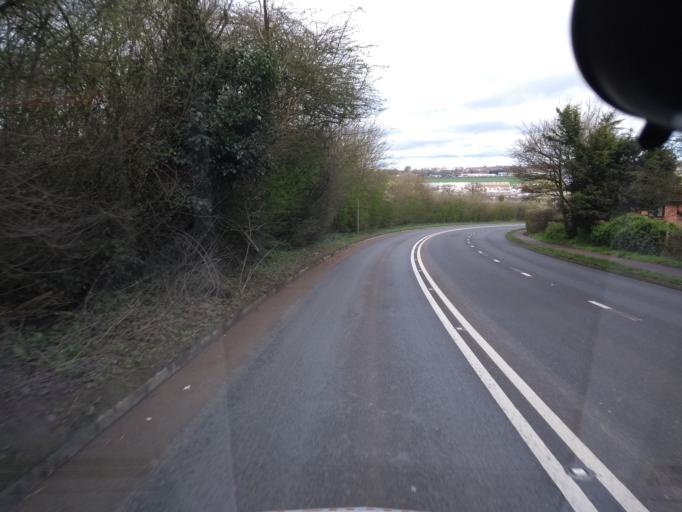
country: GB
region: England
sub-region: Somerset
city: Yeovil
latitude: 50.9297
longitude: -2.6640
